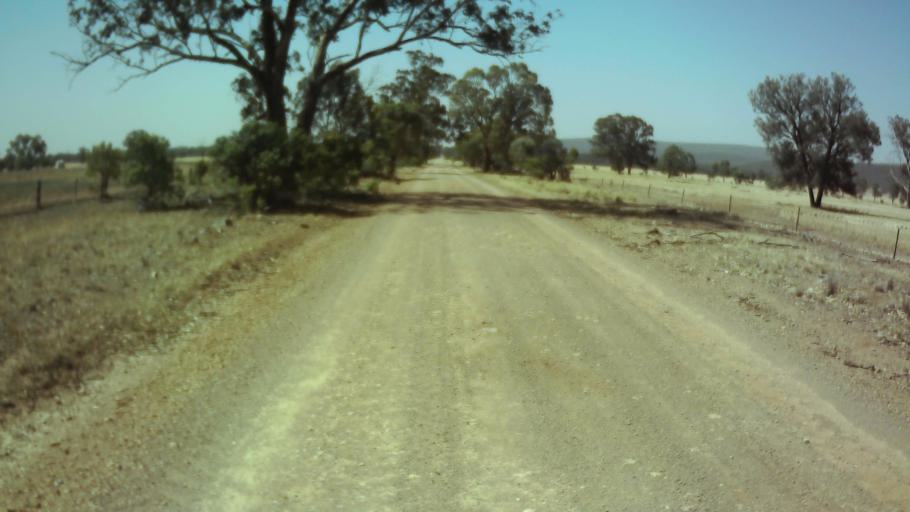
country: AU
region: New South Wales
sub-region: Weddin
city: Grenfell
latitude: -33.9886
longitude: 147.9269
